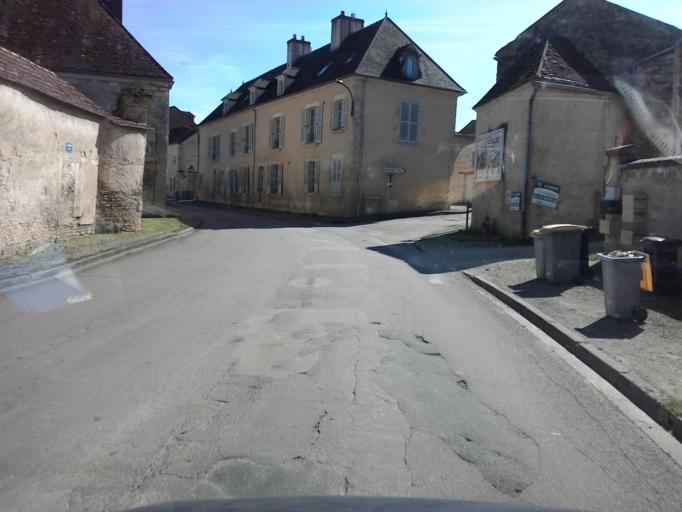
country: FR
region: Bourgogne
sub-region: Departement de l'Yonne
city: Joux-la-Ville
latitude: 47.5580
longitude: 3.8898
